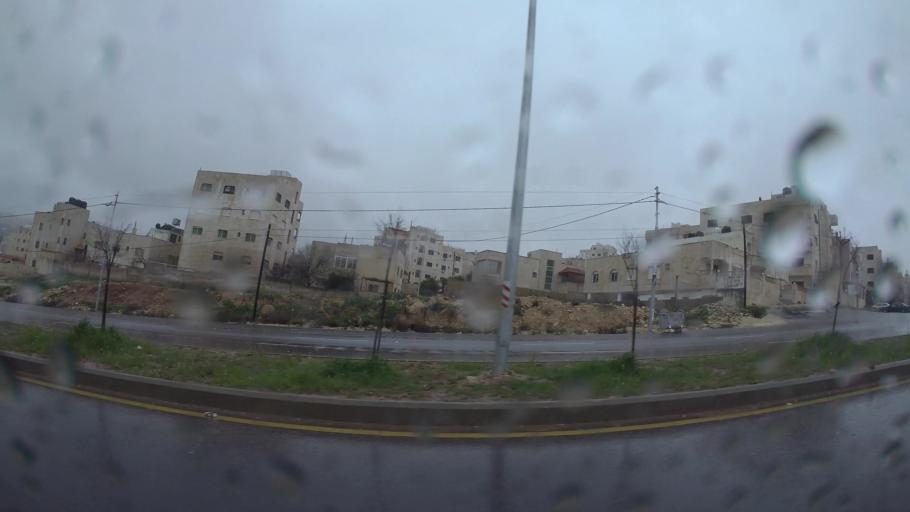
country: JO
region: Amman
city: Al Jubayhah
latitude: 32.0463
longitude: 35.8840
